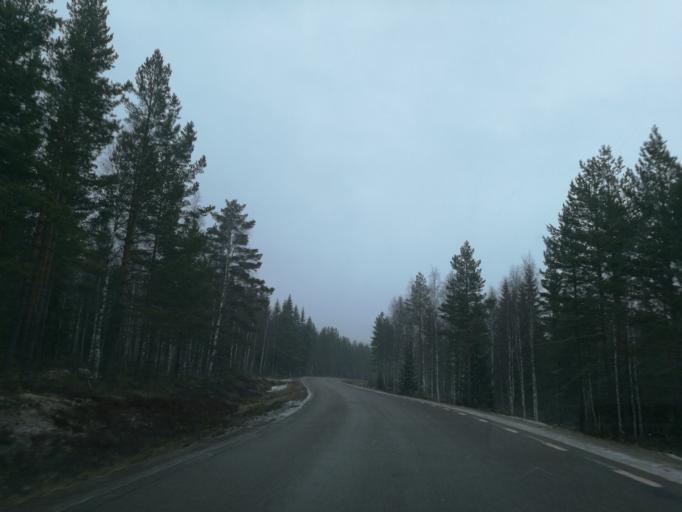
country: NO
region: Hedmark
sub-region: Asnes
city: Flisa
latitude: 60.6973
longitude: 12.5589
